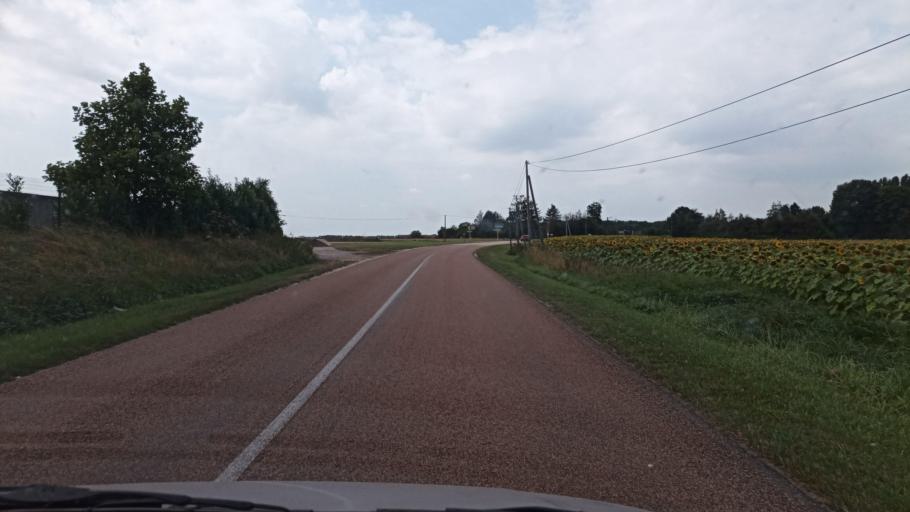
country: FR
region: Bourgogne
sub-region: Departement de l'Yonne
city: Saint-Julien-du-Sault
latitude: 48.0578
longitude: 3.2383
